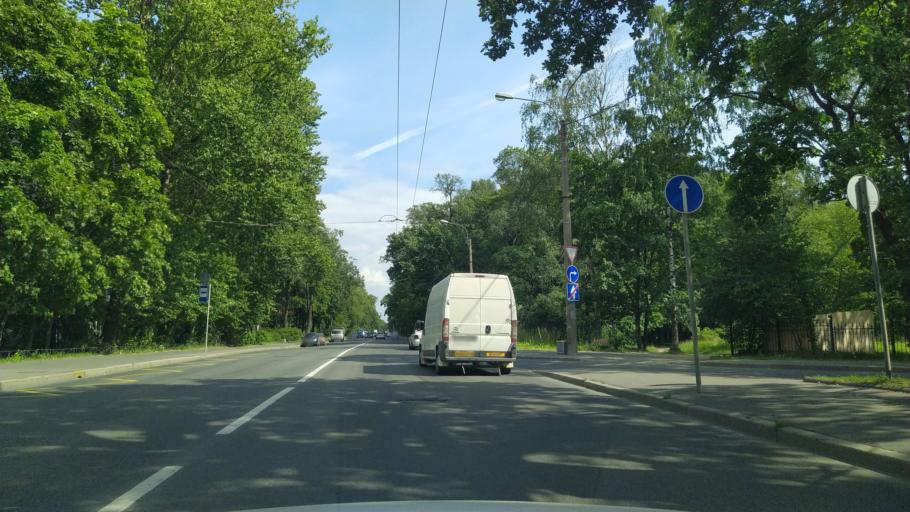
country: RU
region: Leningrad
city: Svetlanovskiy
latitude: 59.9978
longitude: 30.3326
